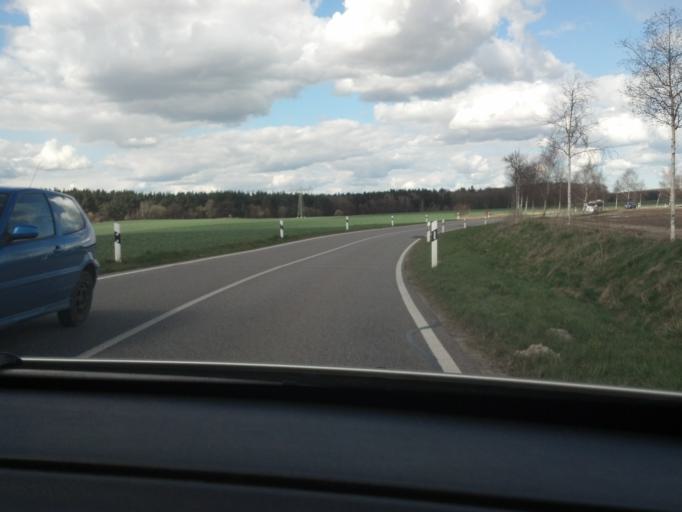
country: DE
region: Mecklenburg-Vorpommern
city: Burg Stargard
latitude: 53.5123
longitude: 13.3174
